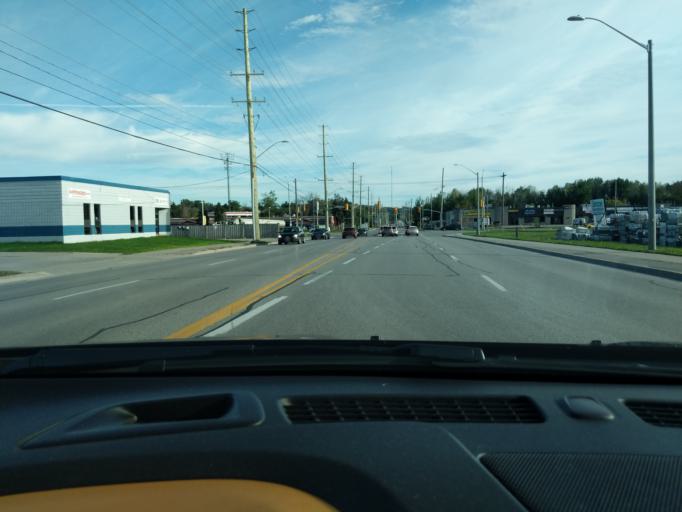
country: CA
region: Ontario
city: Barrie
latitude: 44.3771
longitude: -79.7210
